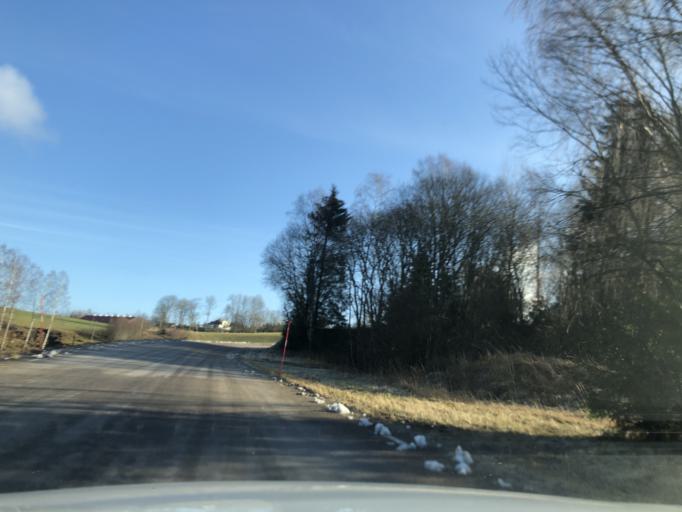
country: SE
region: Vaestra Goetaland
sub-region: Ulricehamns Kommun
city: Ulricehamn
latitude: 57.8050
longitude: 13.5463
